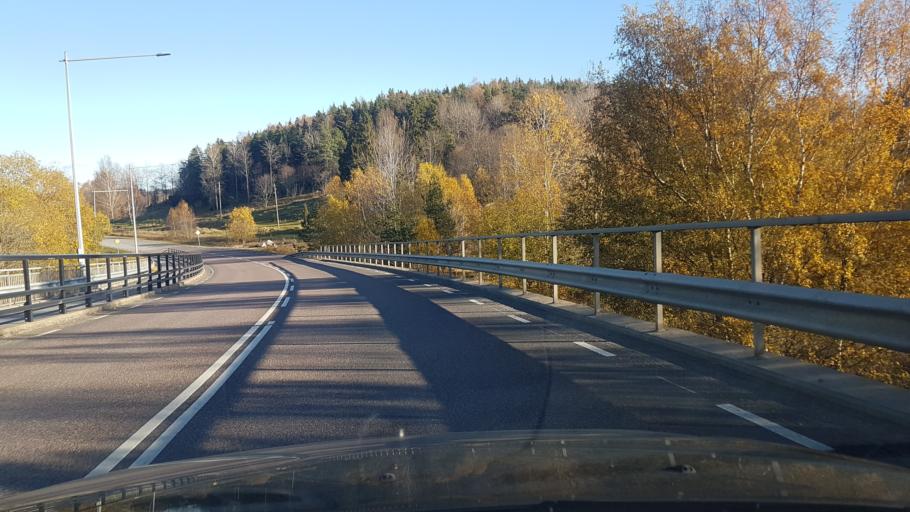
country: SE
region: Stockholm
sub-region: Sigtuna Kommun
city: Marsta
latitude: 59.6236
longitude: 17.8626
